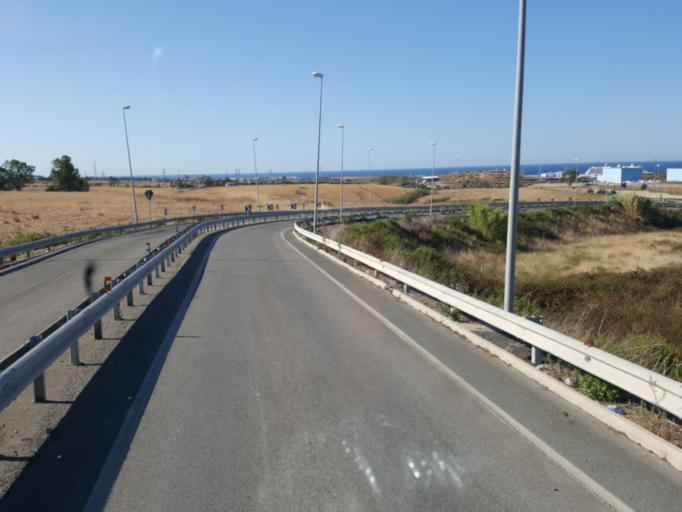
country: IT
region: Latium
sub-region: Citta metropolitana di Roma Capitale
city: Aurelia
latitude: 42.1293
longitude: 11.7942
